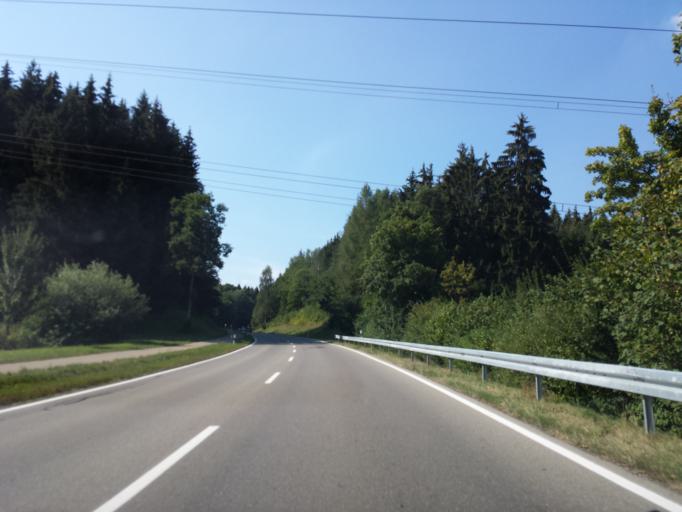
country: DE
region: Bavaria
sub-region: Swabia
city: Deisenhausen
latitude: 48.2620
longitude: 10.3490
